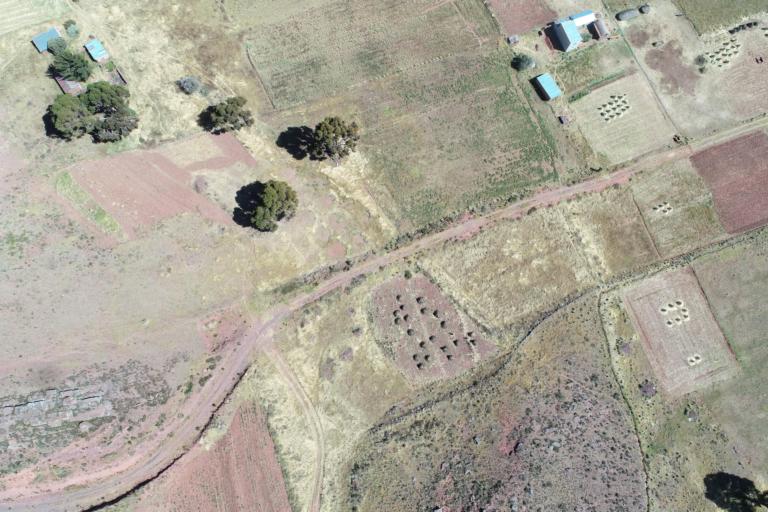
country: BO
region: La Paz
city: Tiahuanaco
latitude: -16.6043
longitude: -68.7812
